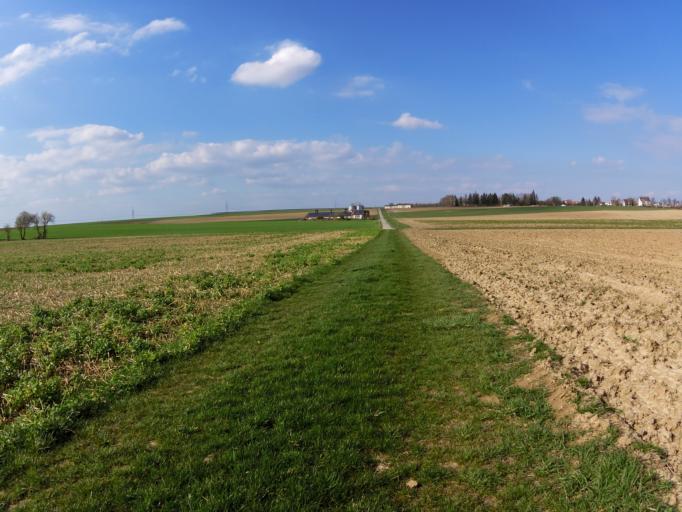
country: DE
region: Bavaria
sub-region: Regierungsbezirk Unterfranken
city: Biebelried
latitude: 49.7887
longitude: 10.0816
